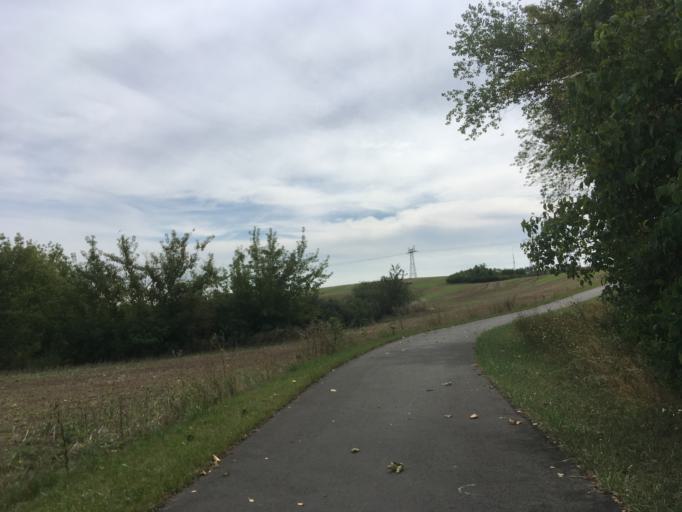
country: DE
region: Brandenburg
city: Mittenwalde
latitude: 53.2398
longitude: 13.6479
